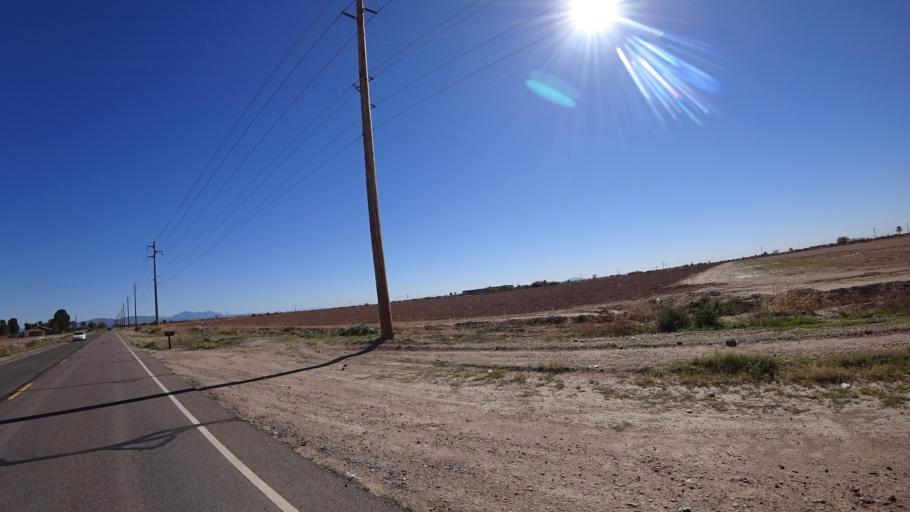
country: US
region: Arizona
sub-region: Maricopa County
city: Scottsdale
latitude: 33.4950
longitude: -111.8706
